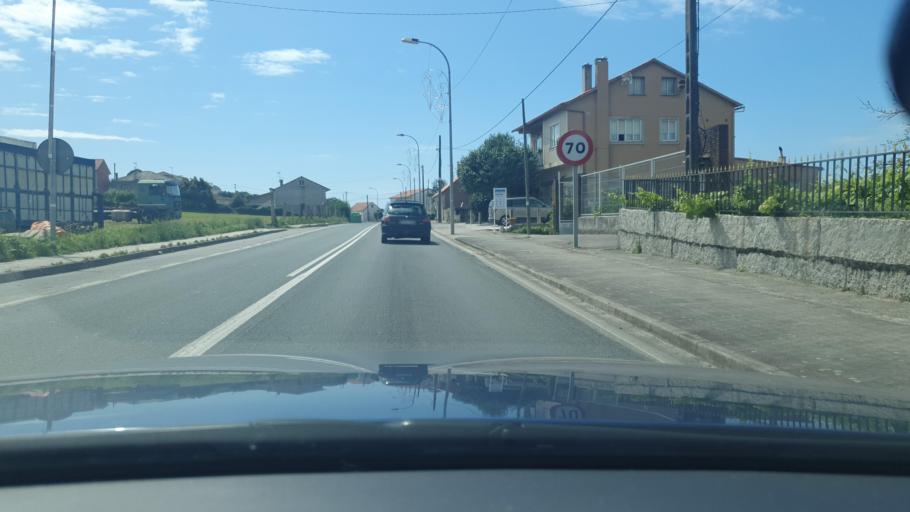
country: ES
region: Galicia
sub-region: Provincia de Pontevedra
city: Sanxenxo
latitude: 42.4410
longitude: -8.8388
